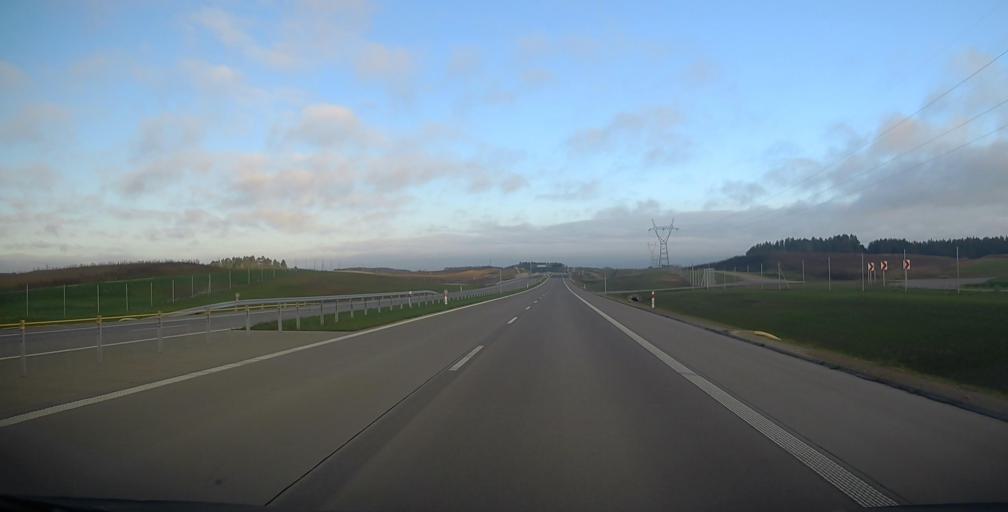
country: PL
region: Podlasie
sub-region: Powiat grajewski
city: Szczuczyn
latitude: 53.6763
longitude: 22.2958
